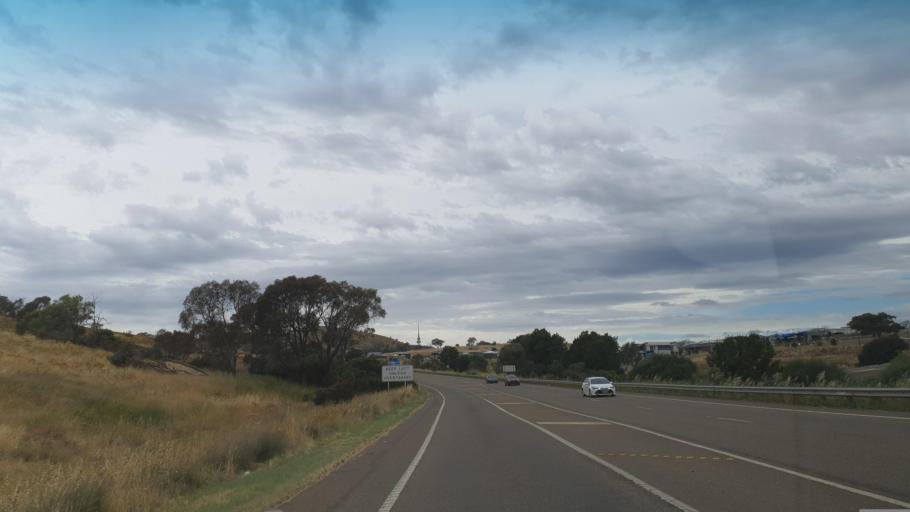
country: AU
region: Australian Capital Territory
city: Macquarie
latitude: -35.2701
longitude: 149.0390
